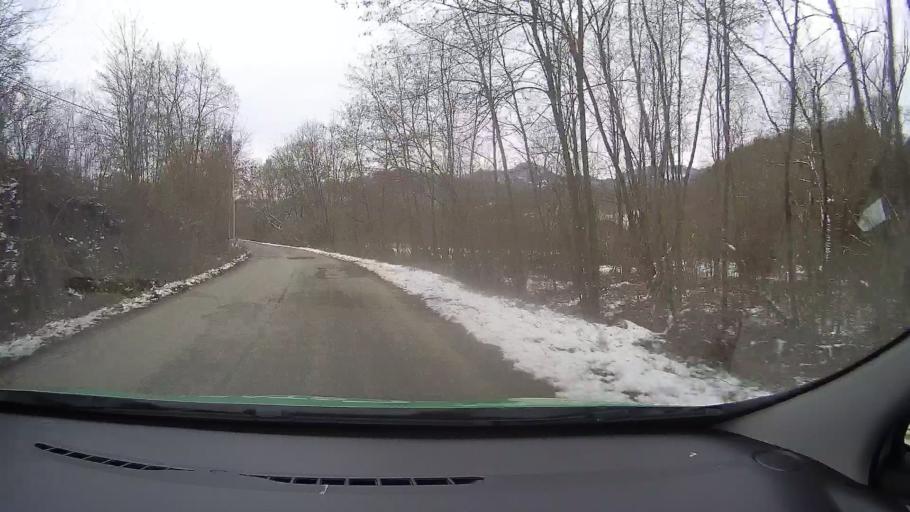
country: RO
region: Hunedoara
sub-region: Comuna Balsa
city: Balsa
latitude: 46.0394
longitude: 23.0746
